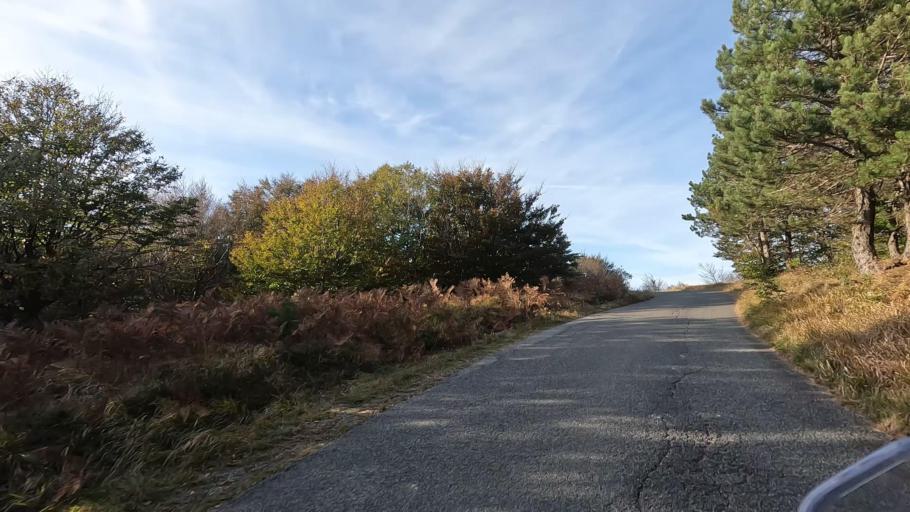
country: IT
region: Liguria
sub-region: Provincia di Genova
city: Sciarborasca
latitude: 44.4303
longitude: 8.5766
